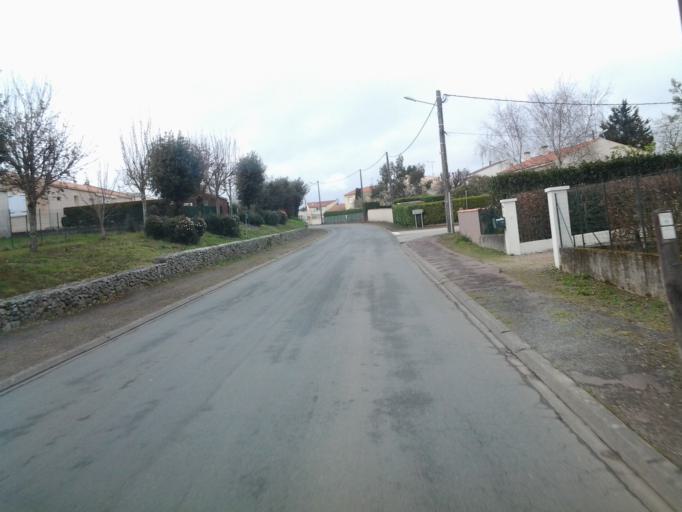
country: FR
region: Pays de la Loire
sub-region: Departement de la Vendee
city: Avrille
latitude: 46.4658
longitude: -1.4899
